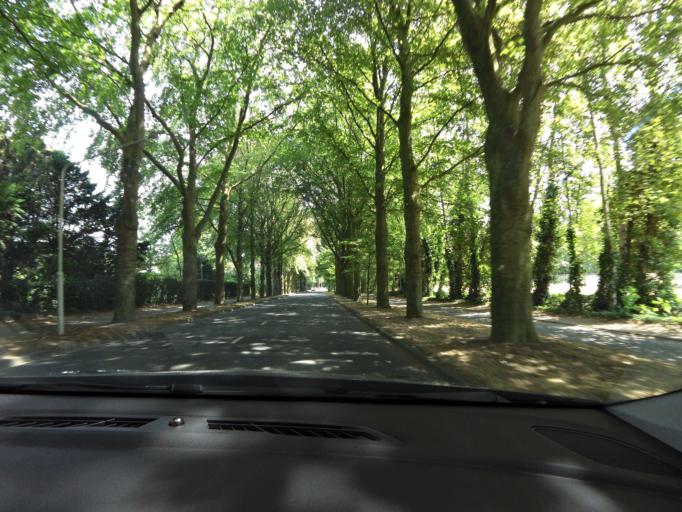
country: NL
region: Limburg
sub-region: Gemeente Weert
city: Weert
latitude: 51.2445
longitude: 5.6818
